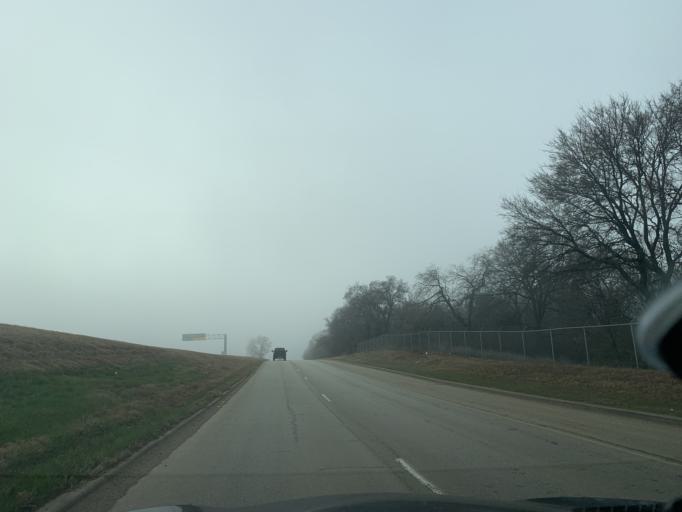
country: US
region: Texas
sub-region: Tarrant County
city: Euless
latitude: 32.8280
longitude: -97.0617
